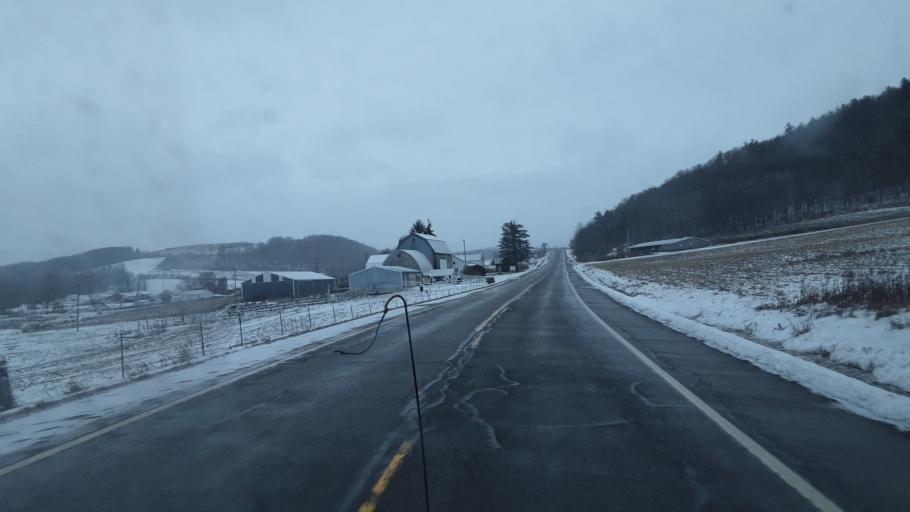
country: US
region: Pennsylvania
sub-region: Tioga County
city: Westfield
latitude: 42.0853
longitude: -77.5412
